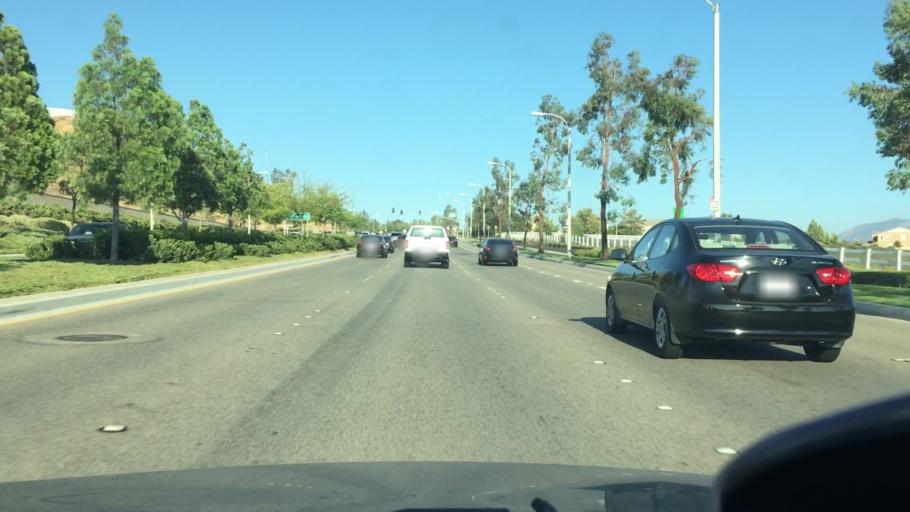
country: US
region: California
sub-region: Los Angeles County
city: Santa Clarita
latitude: 34.4252
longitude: -118.5319
